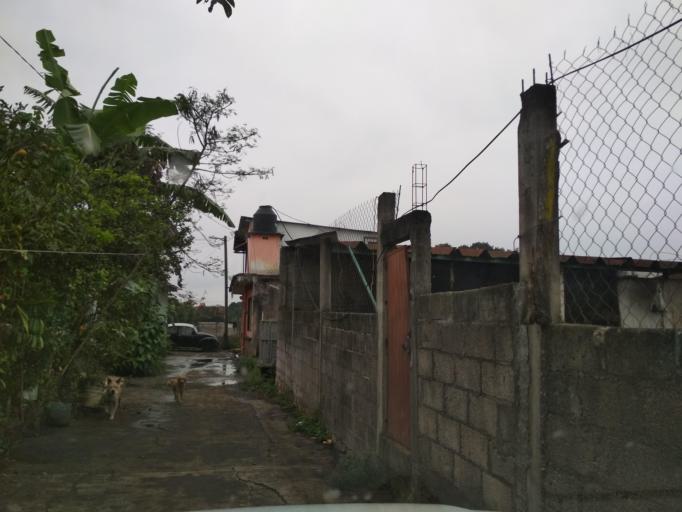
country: MX
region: Veracruz
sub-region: Cordoba
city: Veinte de Noviembre
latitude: 18.8673
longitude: -96.9566
